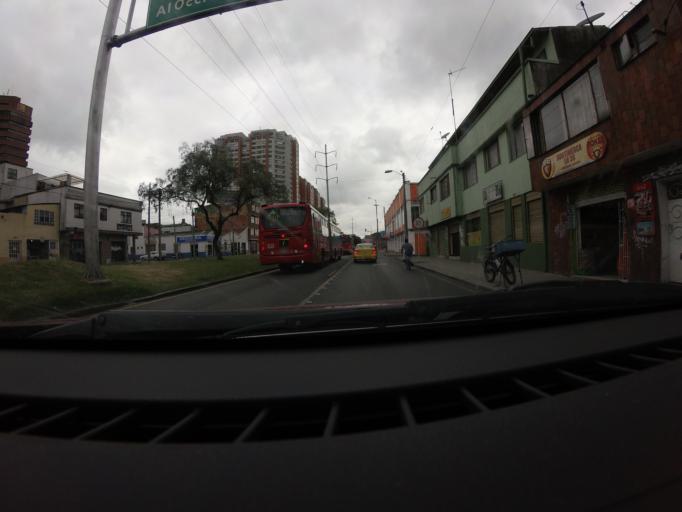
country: CO
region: Bogota D.C.
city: Bogota
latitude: 4.6304
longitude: -74.0826
